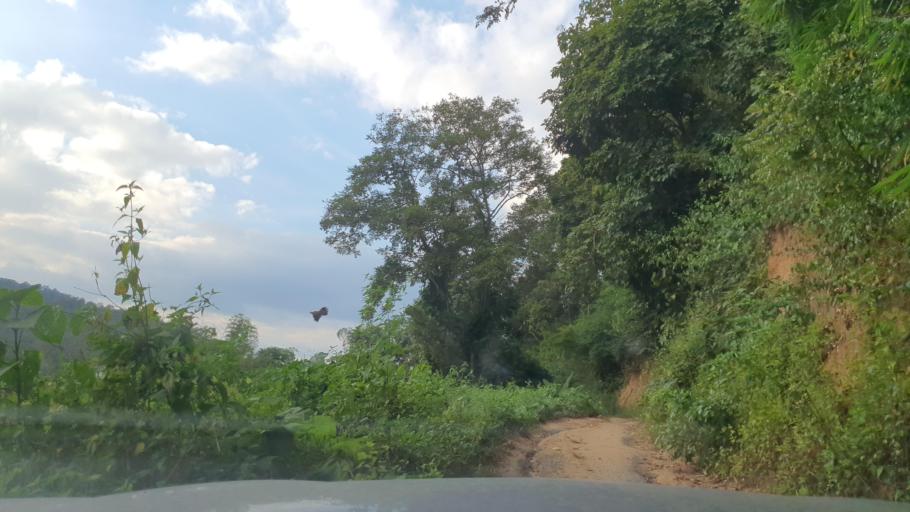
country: TH
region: Chiang Mai
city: Mae On
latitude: 18.8884
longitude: 99.2660
